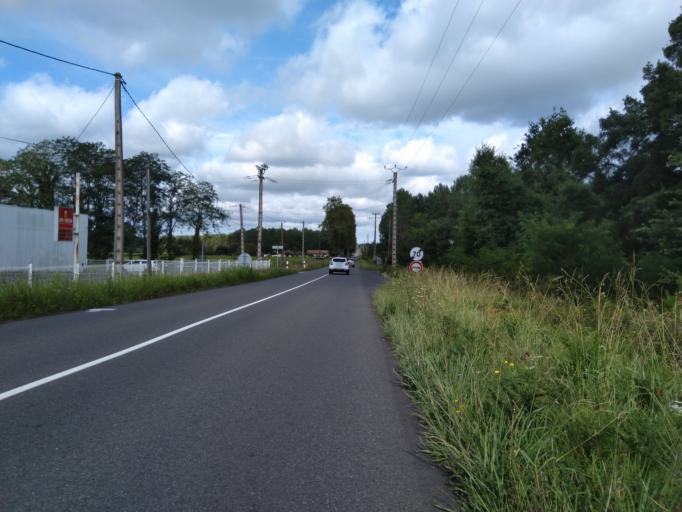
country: FR
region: Aquitaine
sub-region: Departement des Landes
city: Mees
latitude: 43.7344
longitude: -1.1075
